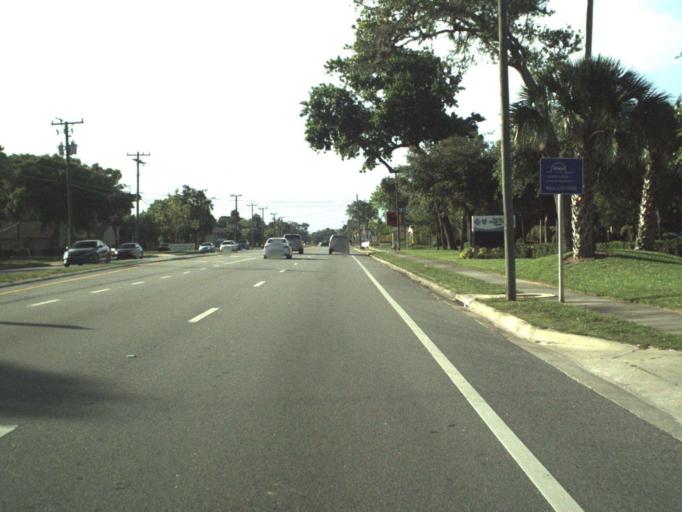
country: US
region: Florida
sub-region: Volusia County
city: Edgewater
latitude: 28.9956
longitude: -80.9097
